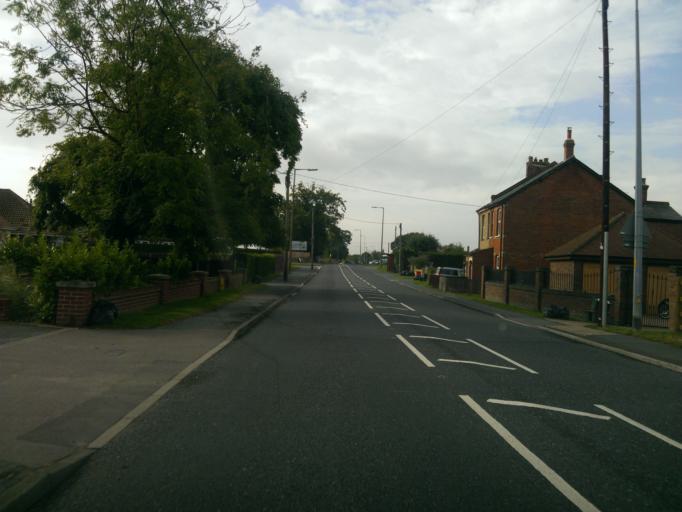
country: GB
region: England
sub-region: Essex
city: Little Clacton
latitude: 51.8231
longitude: 1.1419
